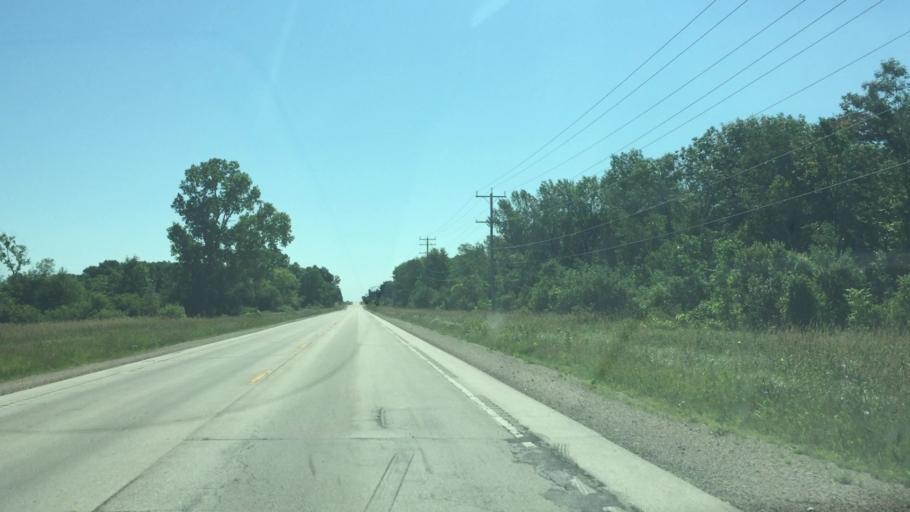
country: US
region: Wisconsin
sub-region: Calumet County
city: Sherwood
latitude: 44.1409
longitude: -88.2529
